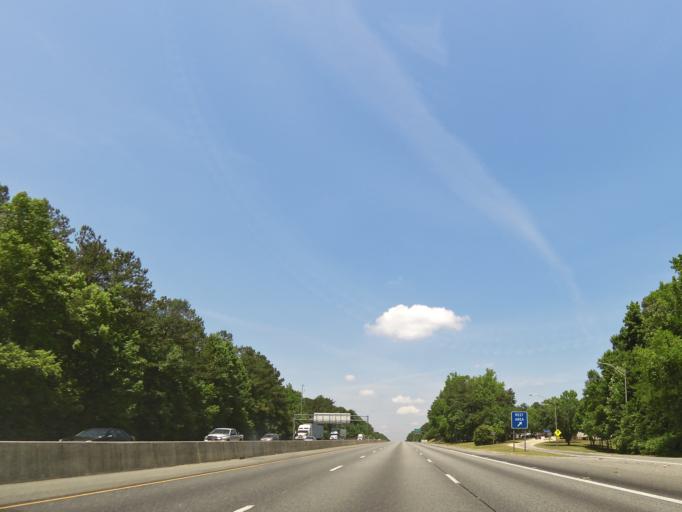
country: US
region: Georgia
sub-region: Bibb County
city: West Point
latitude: 32.8646
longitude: -83.7521
